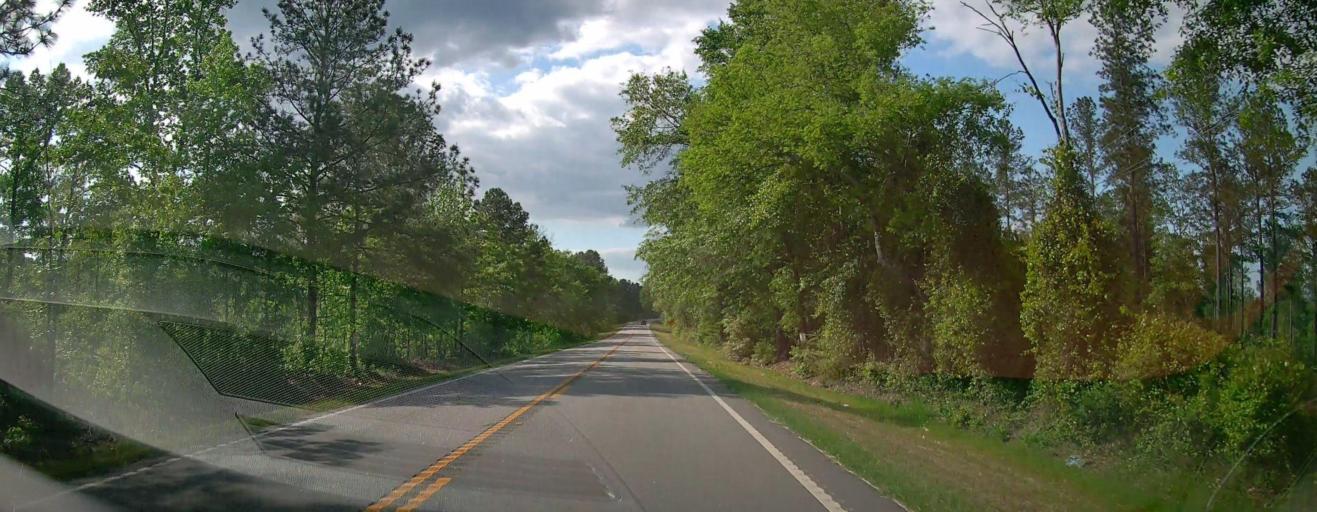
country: US
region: Georgia
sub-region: Baldwin County
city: Hardwick
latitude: 33.0440
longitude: -83.1181
